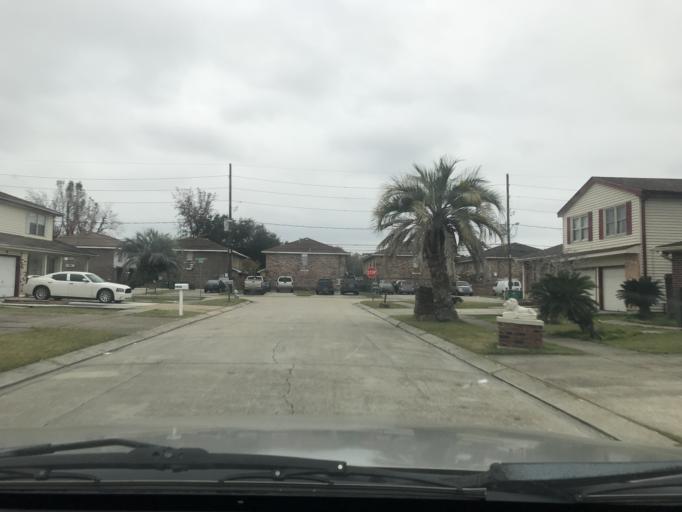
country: US
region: Louisiana
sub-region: Jefferson Parish
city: Woodmere
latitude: 29.8617
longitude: -90.0755
